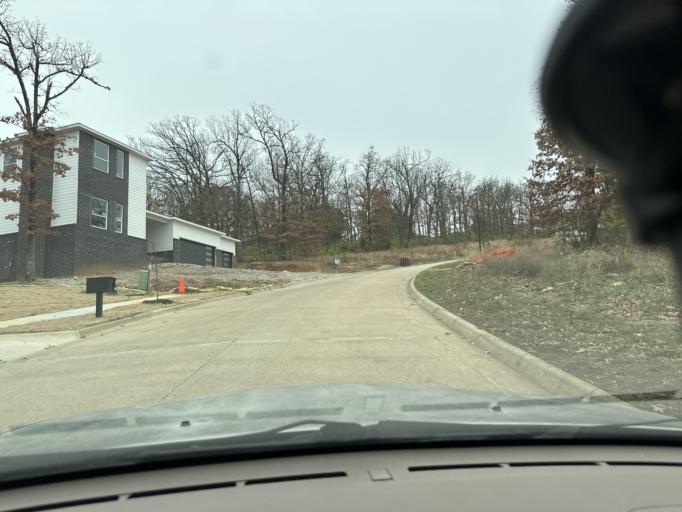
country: US
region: Arkansas
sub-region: Washington County
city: Fayetteville
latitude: 36.0944
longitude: -94.1490
